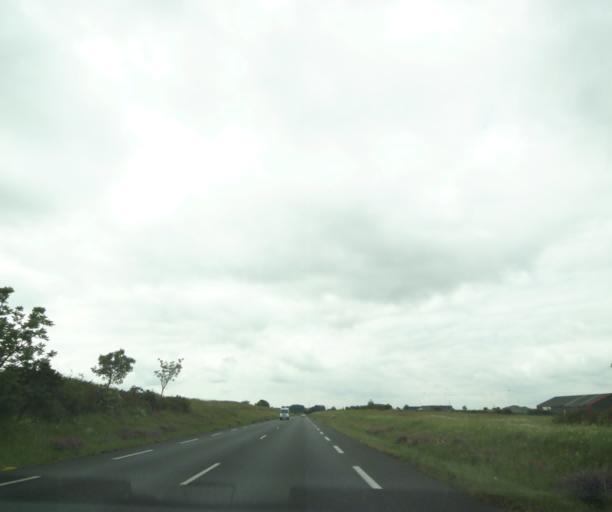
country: FR
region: Pays de la Loire
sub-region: Departement de Maine-et-Loire
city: Distre
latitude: 47.2293
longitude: -0.1142
